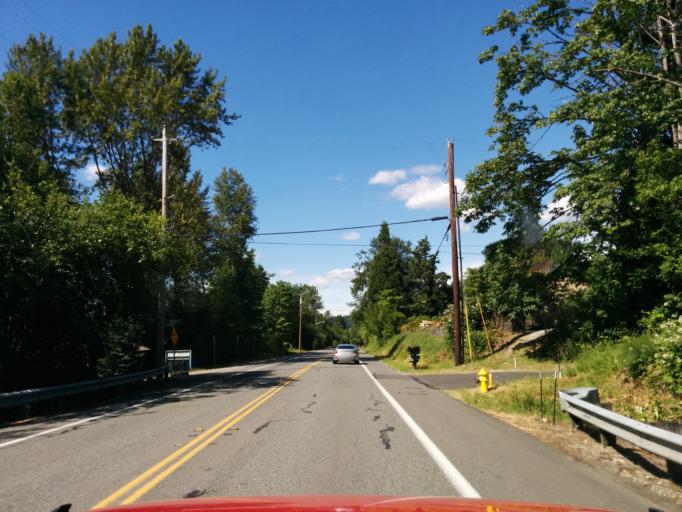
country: US
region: Washington
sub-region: King County
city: West Lake Sammamish
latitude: 47.5986
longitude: -122.0806
